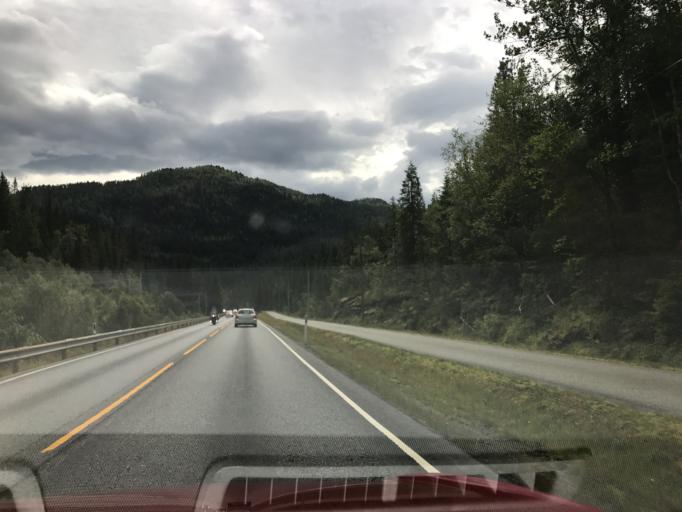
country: NO
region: Hordaland
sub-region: Granvin
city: Granvin
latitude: 60.5903
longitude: 6.6014
